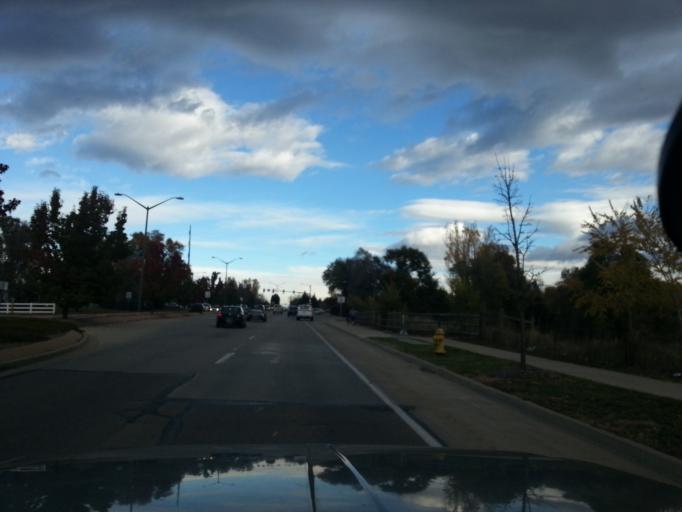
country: US
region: Colorado
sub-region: Larimer County
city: Fort Collins
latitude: 40.5513
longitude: -105.1150
